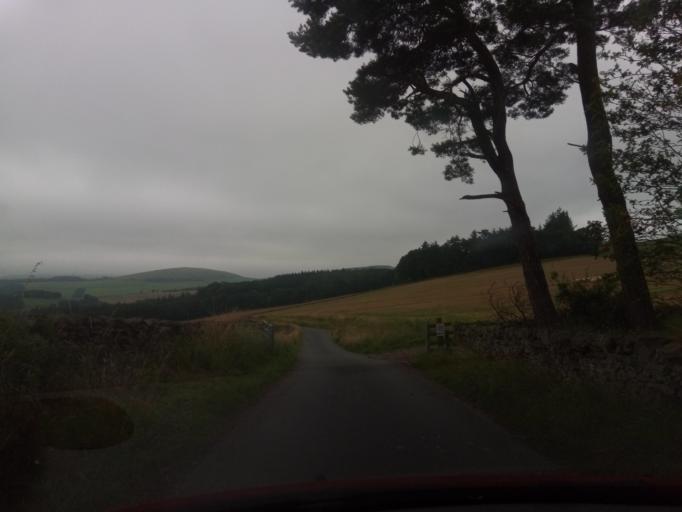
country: GB
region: Scotland
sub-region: The Scottish Borders
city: Galashiels
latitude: 55.6603
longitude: -2.8758
